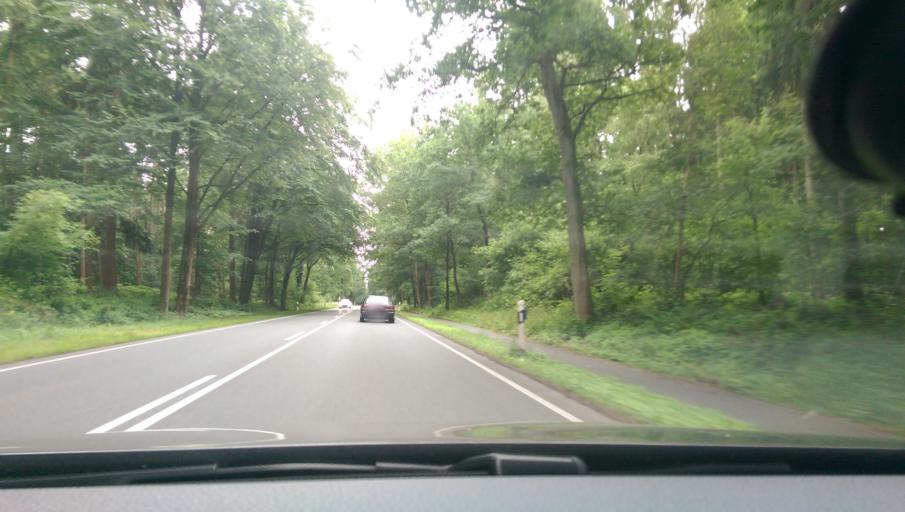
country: DE
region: Lower Saxony
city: Kirchlinteln
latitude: 53.0011
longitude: 9.2695
